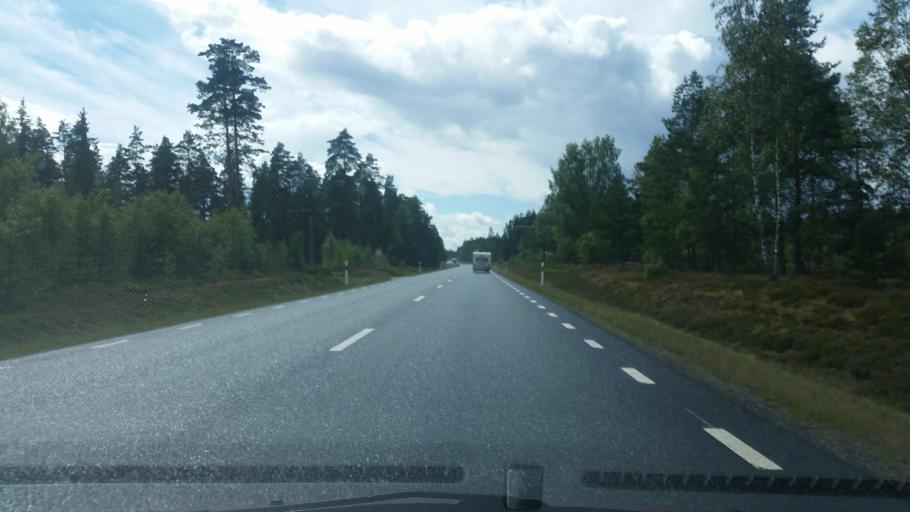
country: SE
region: Joenkoeping
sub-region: Gislaveds Kommun
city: Gislaved
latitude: 57.3982
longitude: 13.5941
